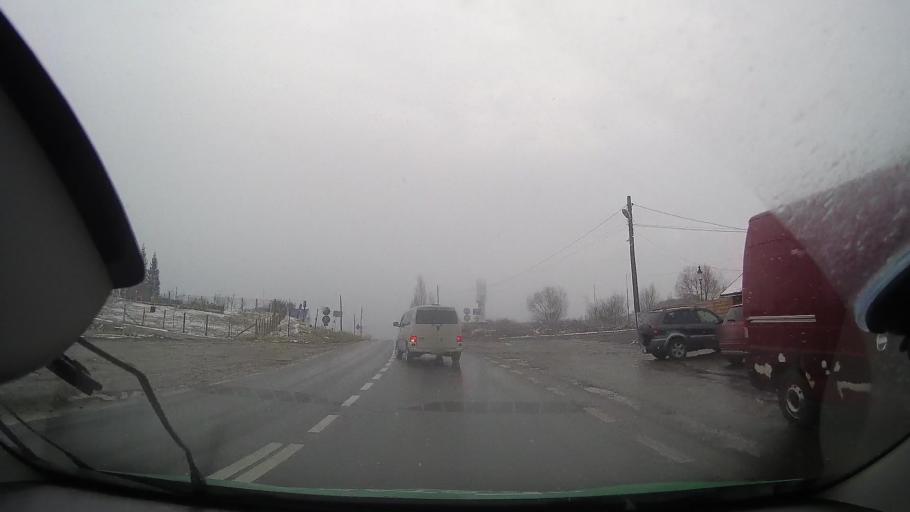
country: RO
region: Sibiu
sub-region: Comuna Blajel
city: Blajel
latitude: 46.2555
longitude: 24.2994
